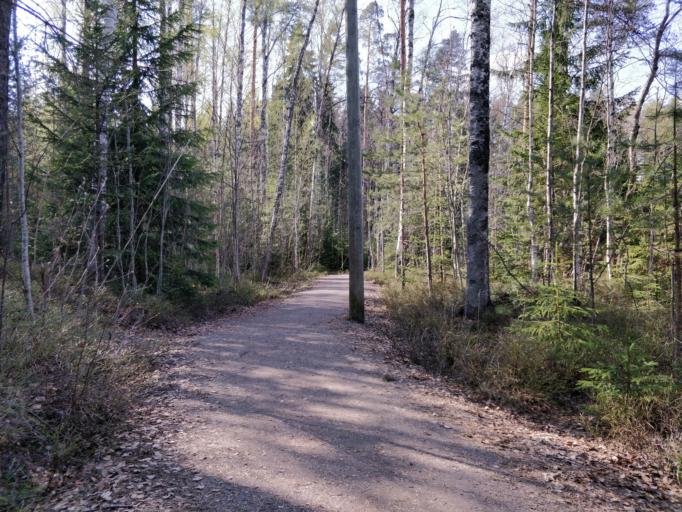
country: FI
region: Uusimaa
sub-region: Helsinki
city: Vantaa
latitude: 60.3114
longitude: 25.1139
